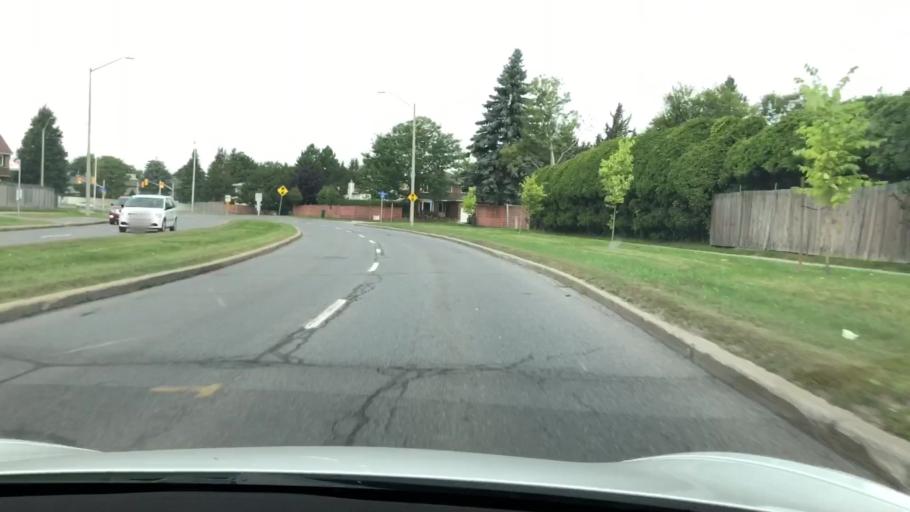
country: CA
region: Quebec
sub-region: Outaouais
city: Gatineau
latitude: 45.4620
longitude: -75.5218
